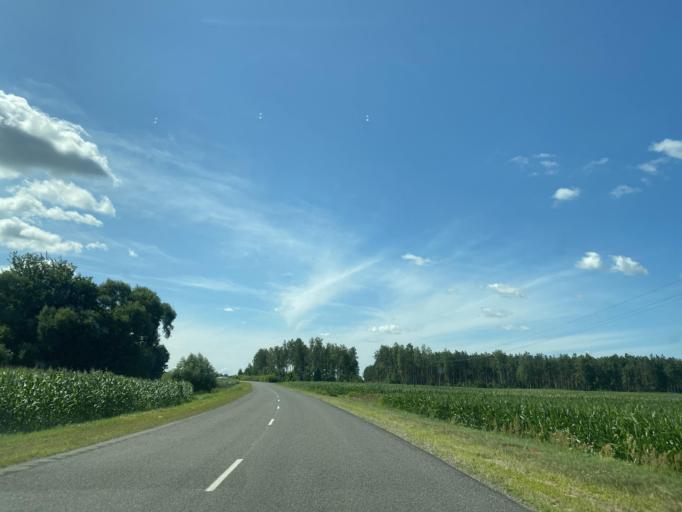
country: BY
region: Brest
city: Ivanava
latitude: 52.2216
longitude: 25.6315
